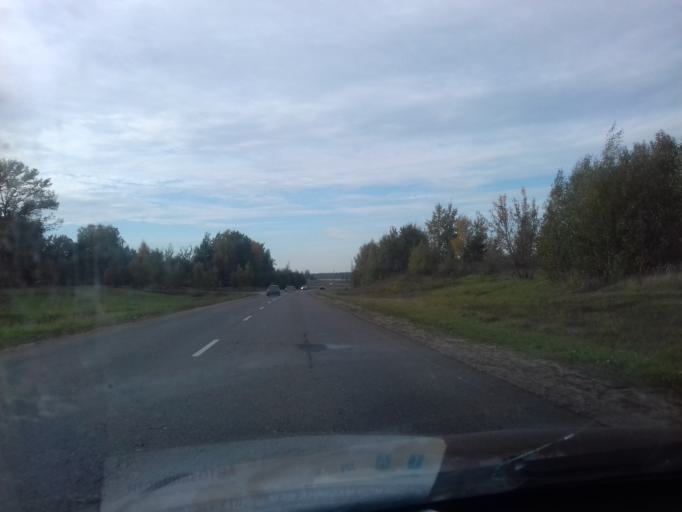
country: BY
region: Minsk
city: Hatava
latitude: 53.7646
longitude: 27.6422
